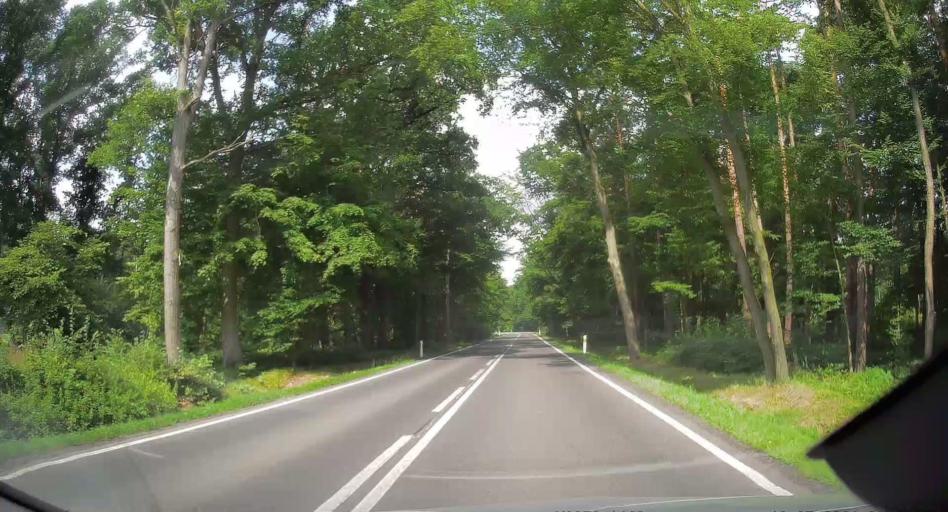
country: PL
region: Opole Voivodeship
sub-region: Powiat prudnicki
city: Twardawa
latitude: 50.3399
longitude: 18.0336
